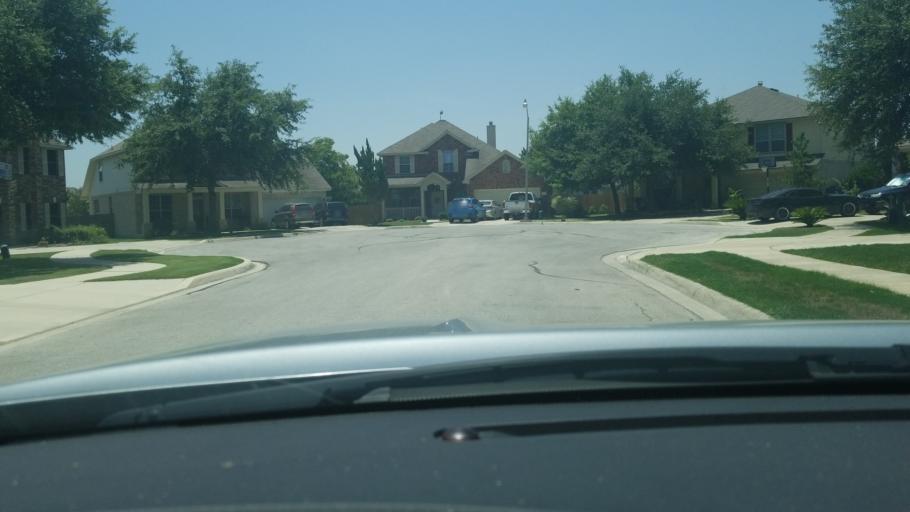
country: US
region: Texas
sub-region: Guadalupe County
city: Cibolo
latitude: 29.5769
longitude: -98.2276
